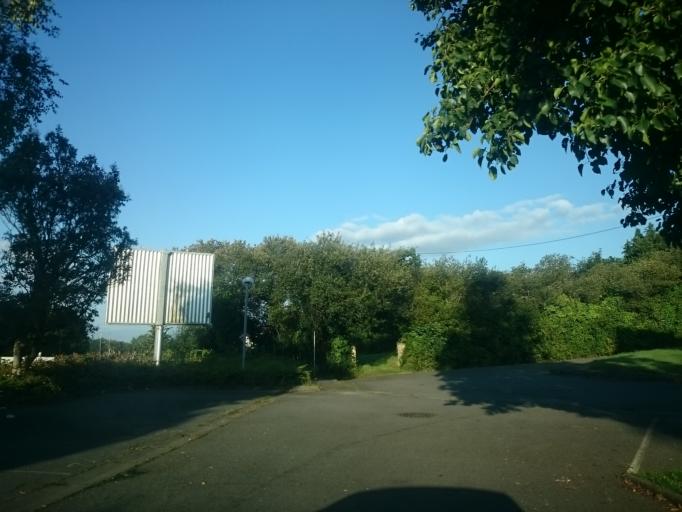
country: FR
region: Brittany
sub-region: Departement du Finistere
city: Brest
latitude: 48.4155
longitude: -4.4774
